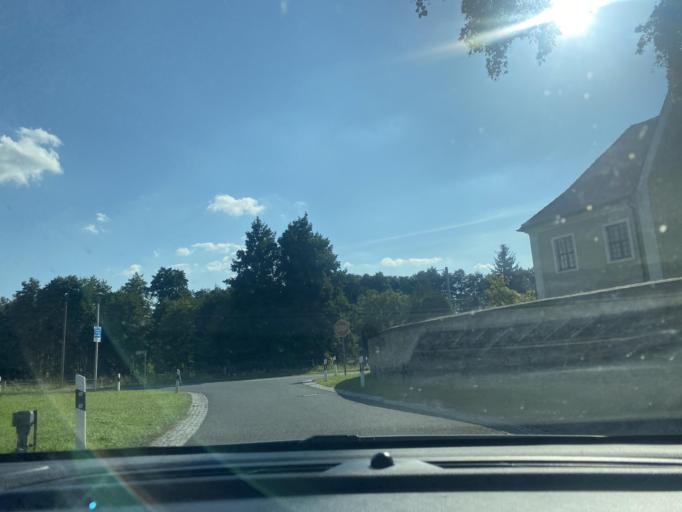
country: DE
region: Saxony
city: Quitzdorf
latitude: 51.2665
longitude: 14.7310
